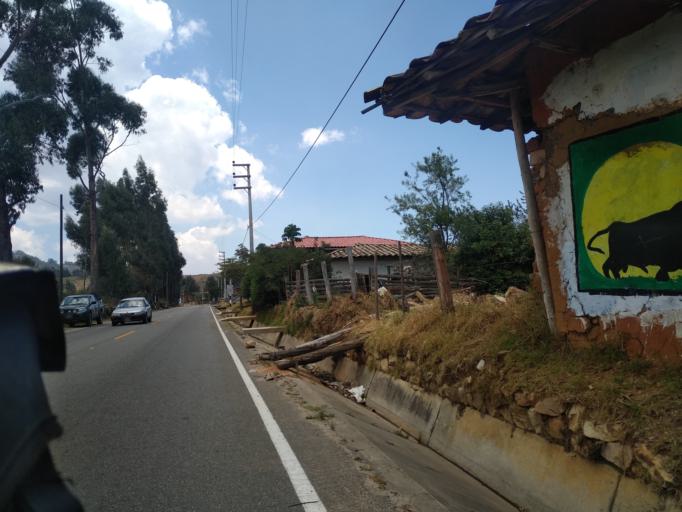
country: PE
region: Cajamarca
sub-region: San Marcos
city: San Marcos
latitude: -7.2831
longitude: -78.2212
